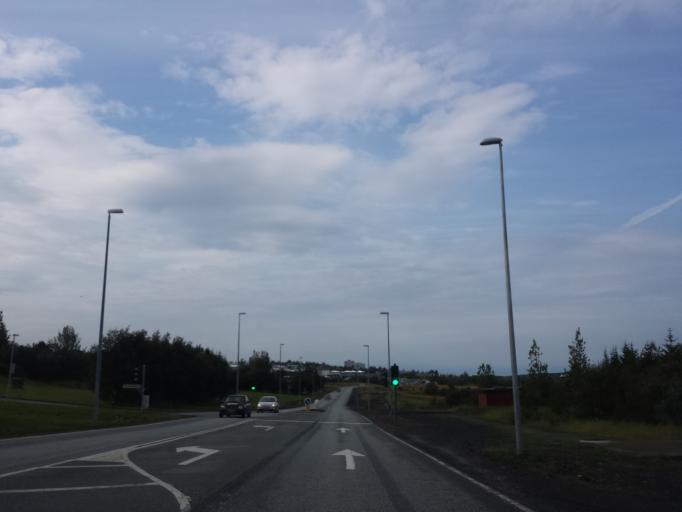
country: IS
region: Capital Region
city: Reykjavik
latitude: 64.1129
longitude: -21.8285
